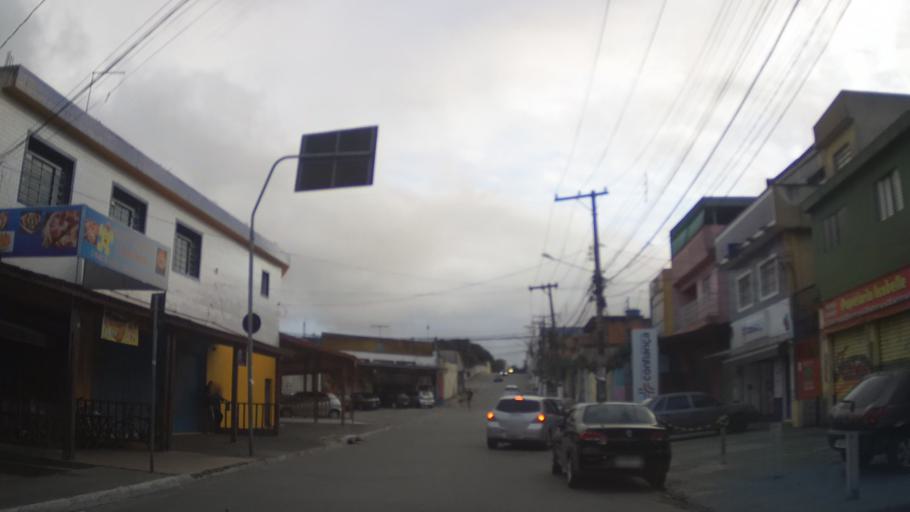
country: BR
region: Sao Paulo
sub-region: Itaquaquecetuba
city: Itaquaquecetuba
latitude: -23.4422
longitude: -46.4266
